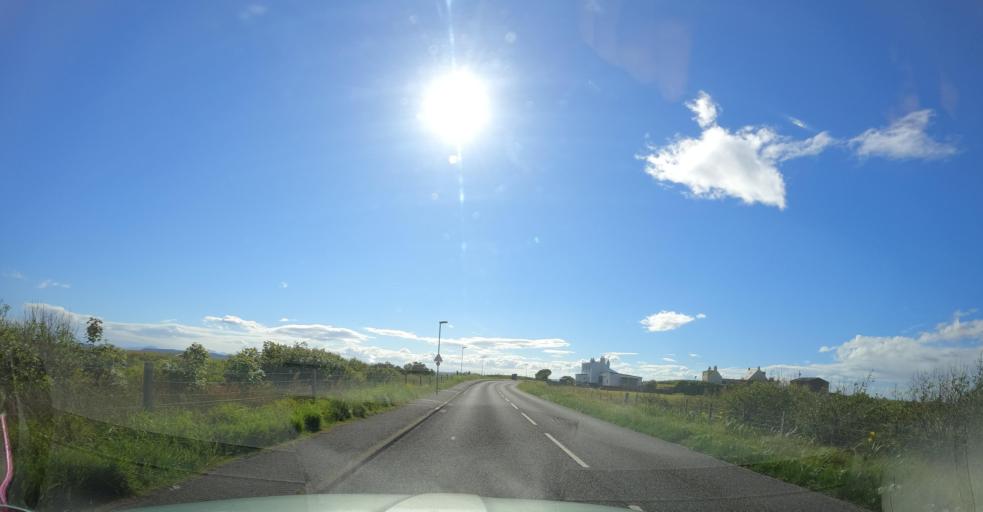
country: GB
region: Scotland
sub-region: Eilean Siar
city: Stornoway
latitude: 58.2047
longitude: -6.2827
